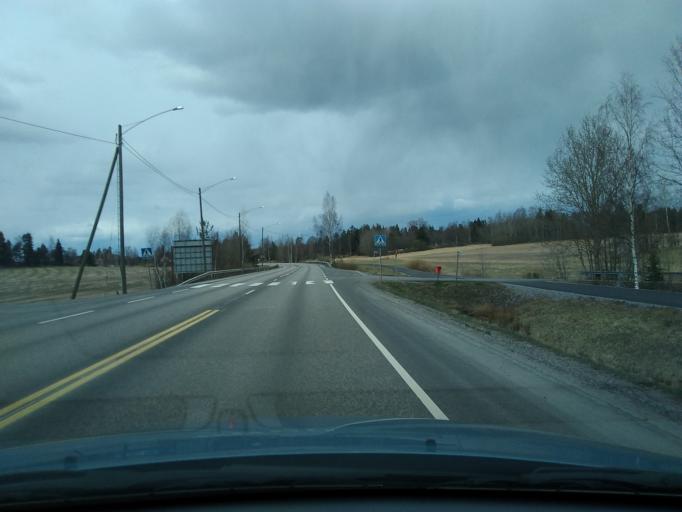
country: FI
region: Uusimaa
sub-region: Helsinki
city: Pornainen
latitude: 60.3336
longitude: 25.4809
